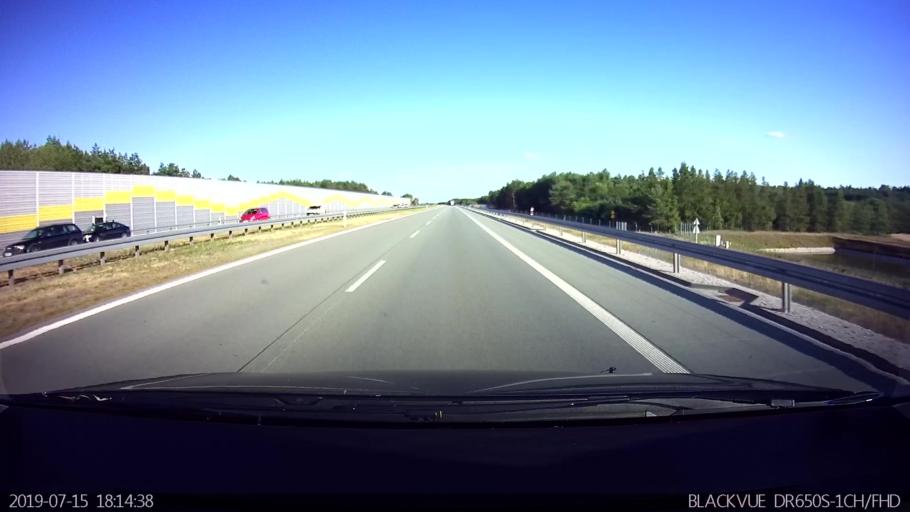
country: PL
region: Lodz Voivodeship
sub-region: Powiat zdunskowolski
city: Zapolice
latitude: 51.5894
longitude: 18.8923
